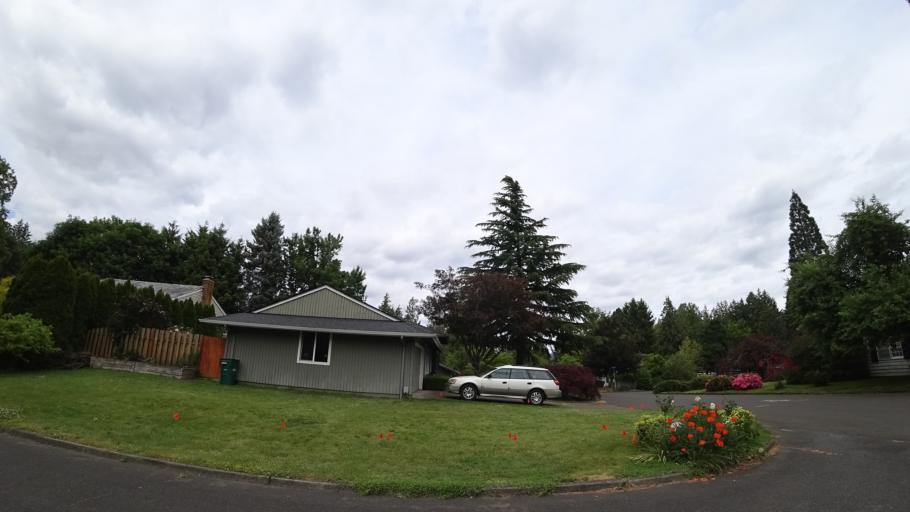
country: US
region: Oregon
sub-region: Washington County
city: Garden Home-Whitford
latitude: 45.4615
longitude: -122.7684
